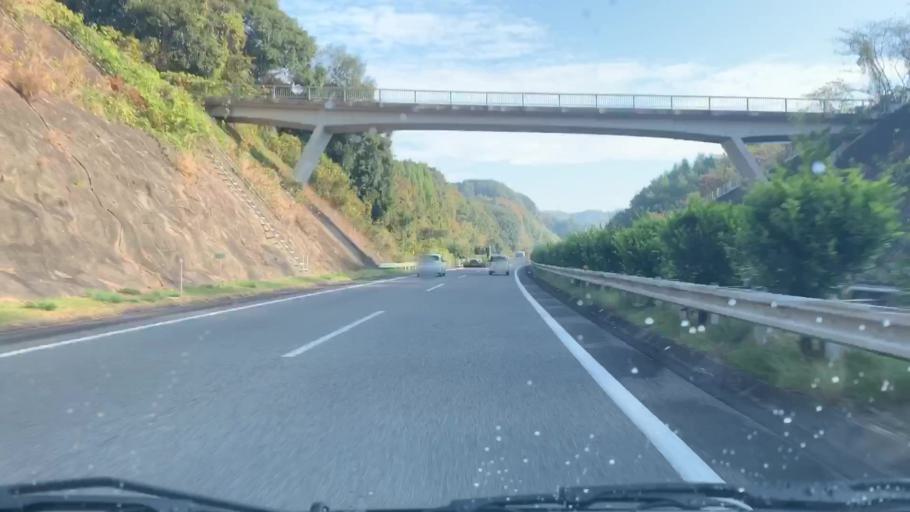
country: JP
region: Saga Prefecture
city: Takeocho-takeo
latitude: 33.2302
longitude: 130.0537
